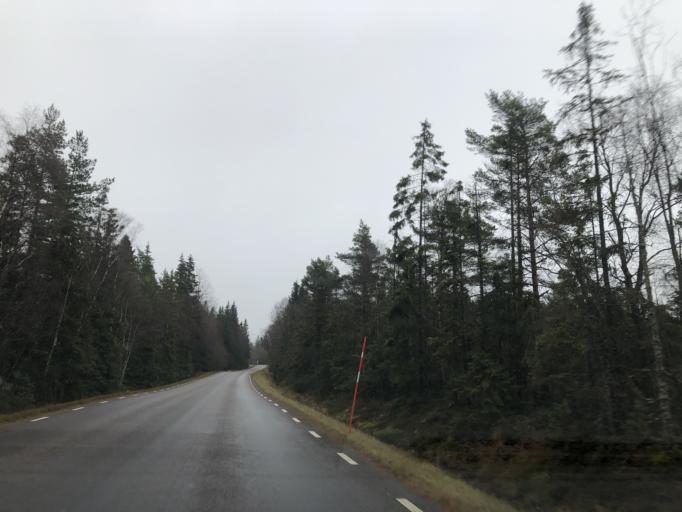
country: SE
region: Vaestra Goetaland
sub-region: Ulricehamns Kommun
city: Ulricehamn
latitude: 57.7558
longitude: 13.5064
